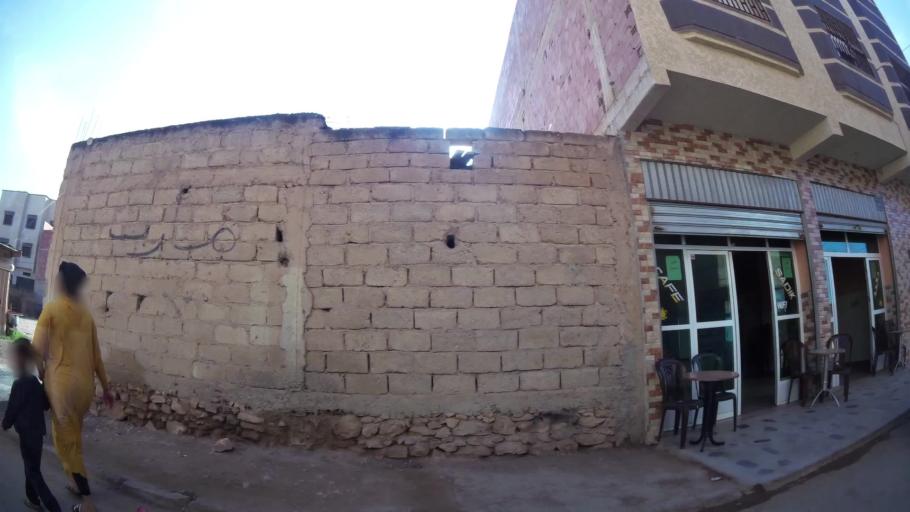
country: MA
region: Oriental
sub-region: Oujda-Angad
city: Oujda
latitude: 34.7157
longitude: -1.9059
